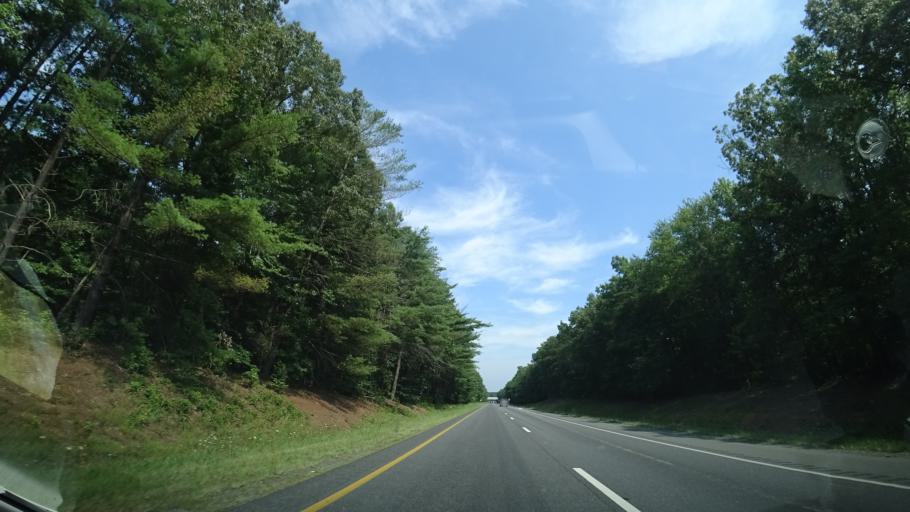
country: US
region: Virginia
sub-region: Louisa County
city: Louisa
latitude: 37.9355
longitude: -78.0994
